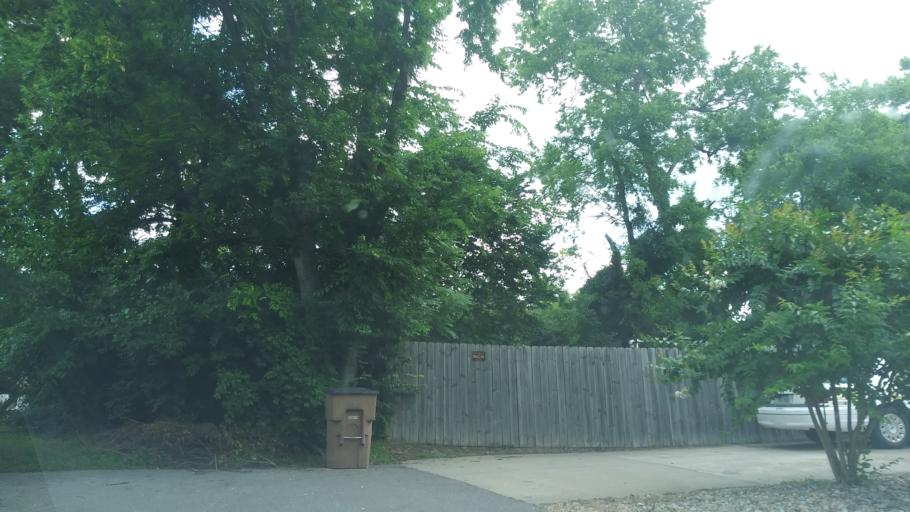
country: US
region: Tennessee
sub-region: Davidson County
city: Nashville
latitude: 36.1433
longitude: -86.8294
